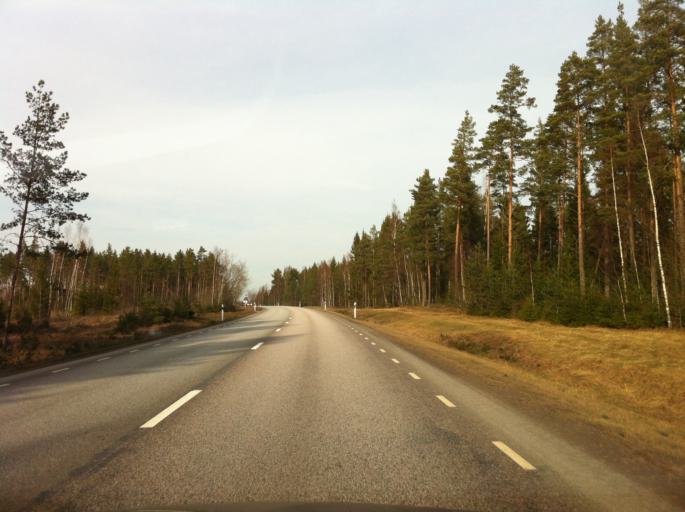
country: SE
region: Vaestra Goetaland
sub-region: Mariestads Kommun
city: Mariestad
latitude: 58.7834
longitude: 13.9658
